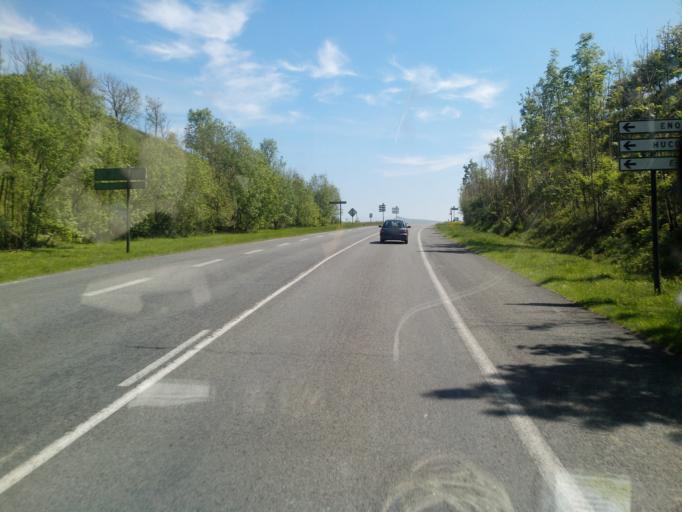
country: FR
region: Nord-Pas-de-Calais
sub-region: Departement du Pas-de-Calais
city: Samer
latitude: 50.5724
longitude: 1.7493
